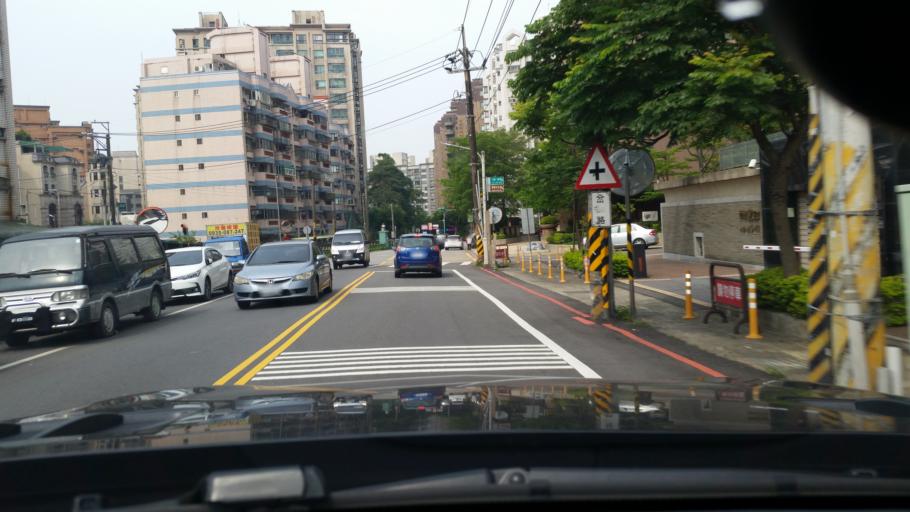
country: TW
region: Taiwan
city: Taoyuan City
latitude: 25.0614
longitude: 121.2990
